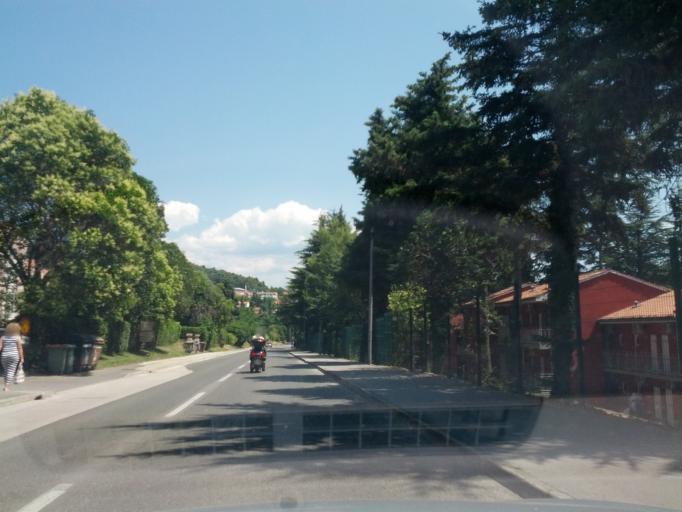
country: SI
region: Koper-Capodistria
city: Ankaran
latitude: 45.5797
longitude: 13.7326
